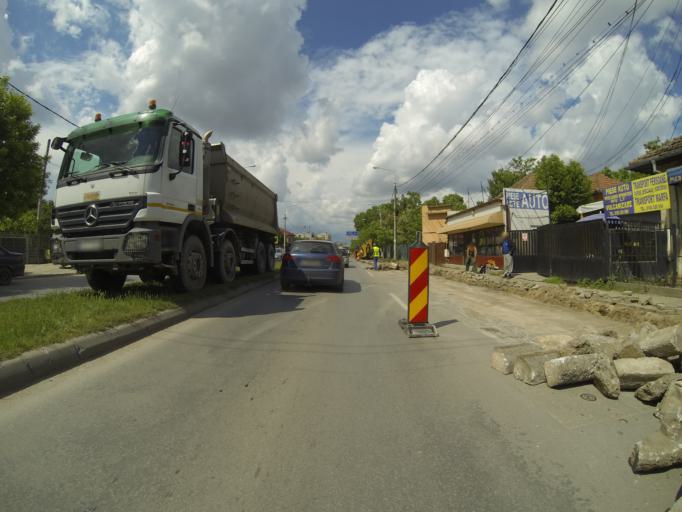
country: RO
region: Dolj
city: Craiova
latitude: 44.2980
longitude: 23.7989
